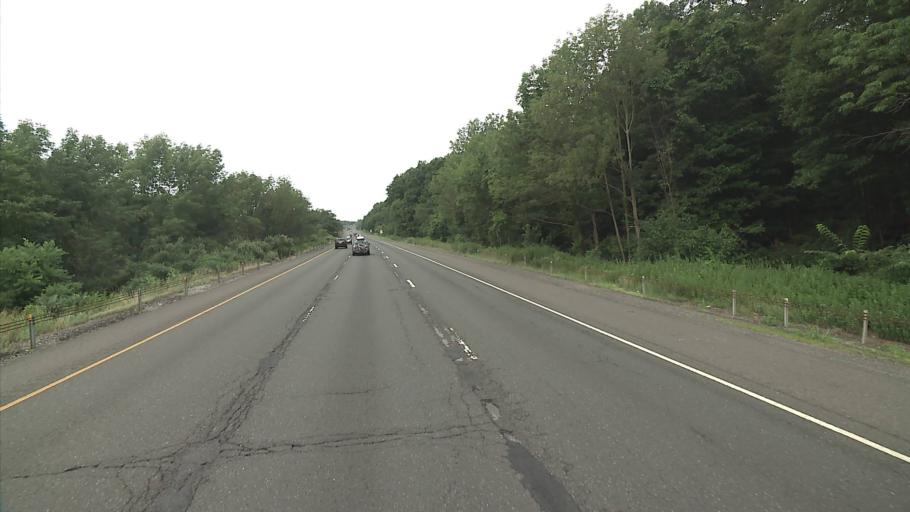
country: US
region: Connecticut
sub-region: Fairfield County
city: Newtown
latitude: 41.4233
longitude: -73.2581
